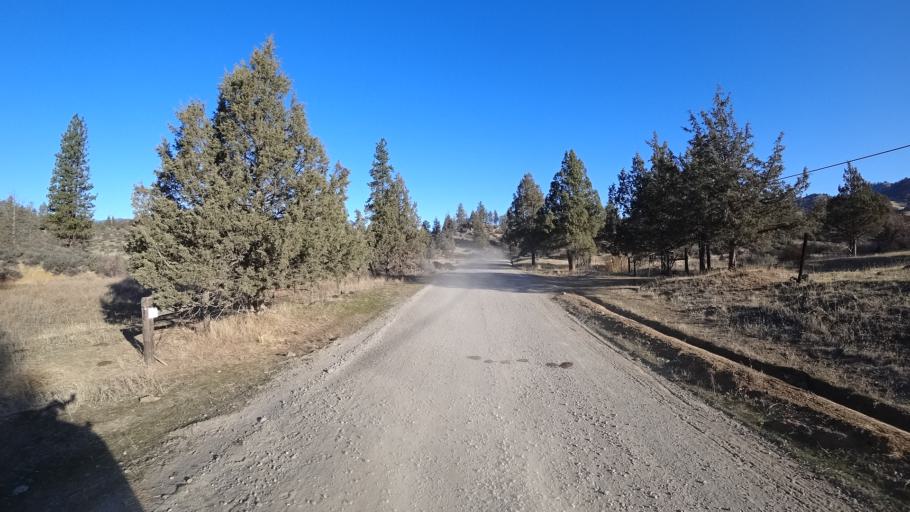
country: US
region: Oregon
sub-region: Jackson County
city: Ashland
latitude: 41.9850
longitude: -122.6232
